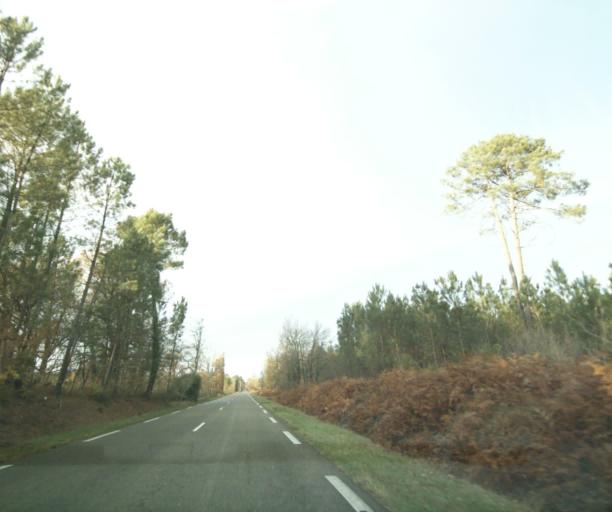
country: FR
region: Aquitaine
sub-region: Departement des Landes
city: Gabarret
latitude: 44.0502
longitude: -0.0420
